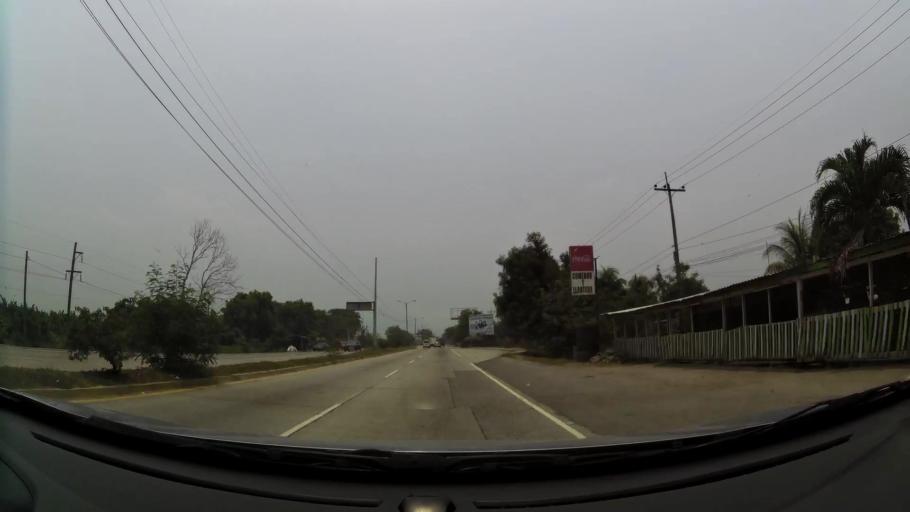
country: HN
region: Yoro
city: El Progreso
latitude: 15.4087
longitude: -87.8356
